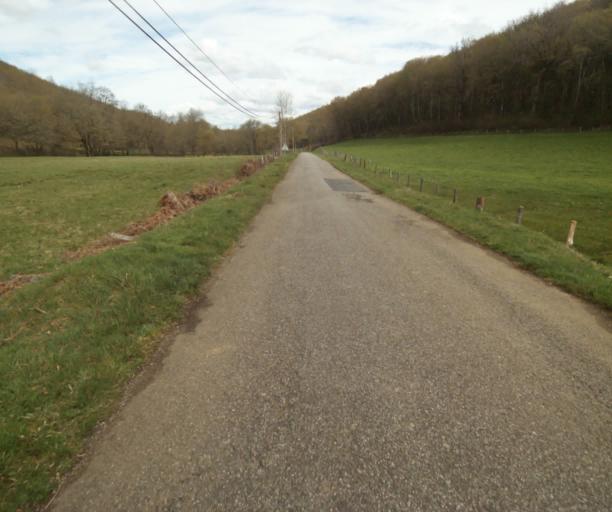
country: FR
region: Limousin
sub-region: Departement de la Correze
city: Laguenne
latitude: 45.2365
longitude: 1.8457
